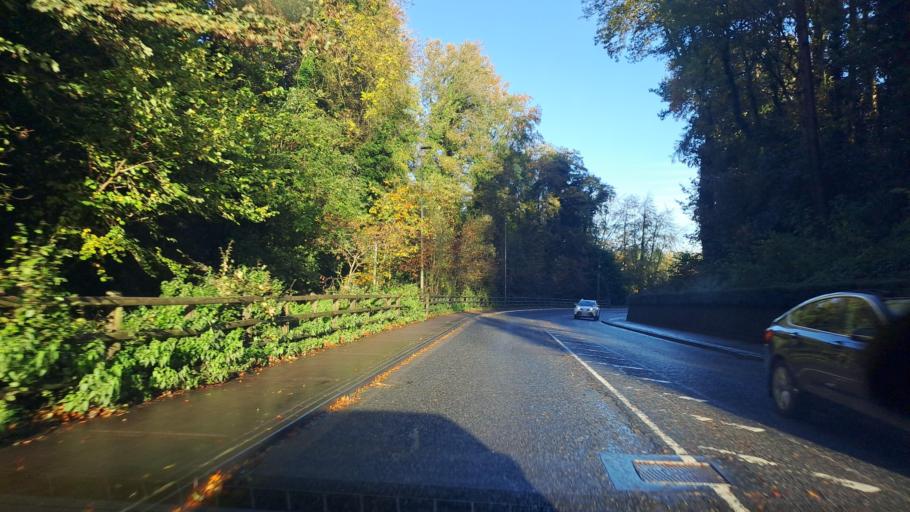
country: IE
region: Ulster
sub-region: County Monaghan
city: Monaghan
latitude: 54.2408
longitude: -6.9698
